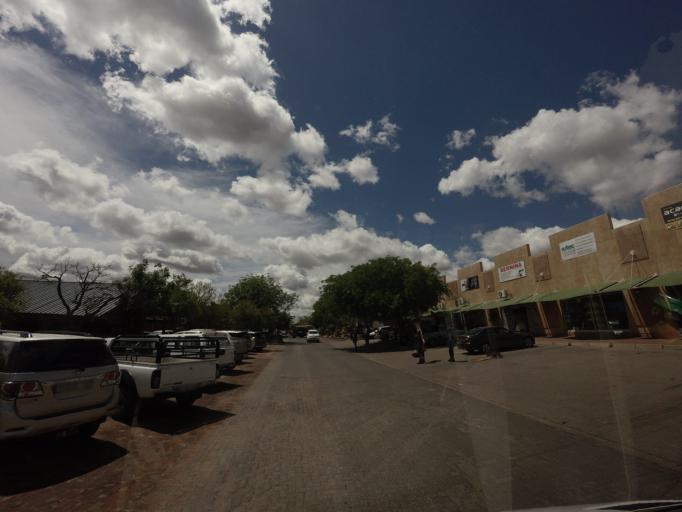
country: ZA
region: Limpopo
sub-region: Mopani District Municipality
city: Hoedspruit
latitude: -24.3503
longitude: 30.9570
